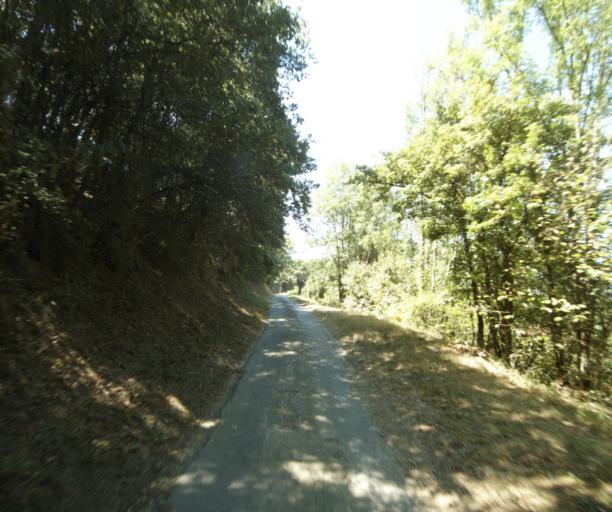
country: FR
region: Rhone-Alpes
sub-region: Departement du Rhone
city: Courzieu
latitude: 45.7472
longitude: 4.5659
